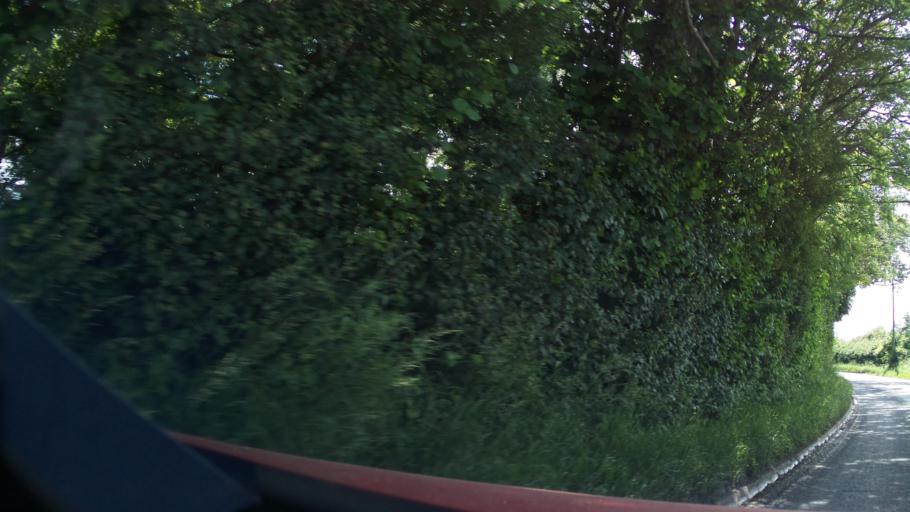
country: GB
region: England
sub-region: Somerset
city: Redlynch
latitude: 51.0587
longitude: -2.4556
